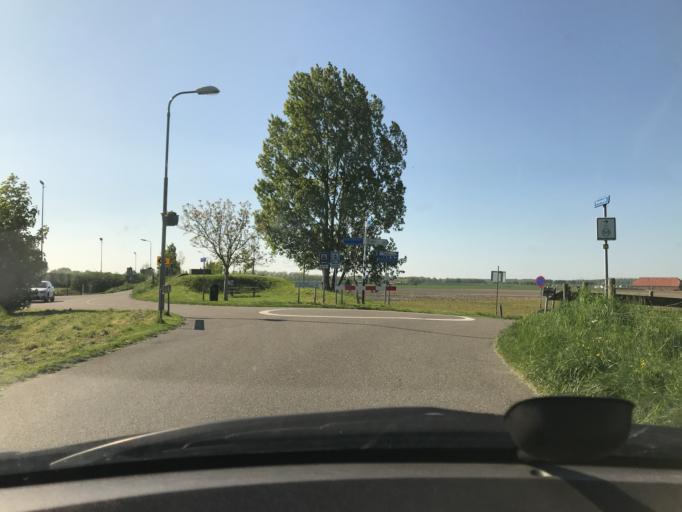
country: NL
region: Zeeland
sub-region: Gemeente Goes
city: Goes
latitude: 51.5305
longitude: 3.8153
